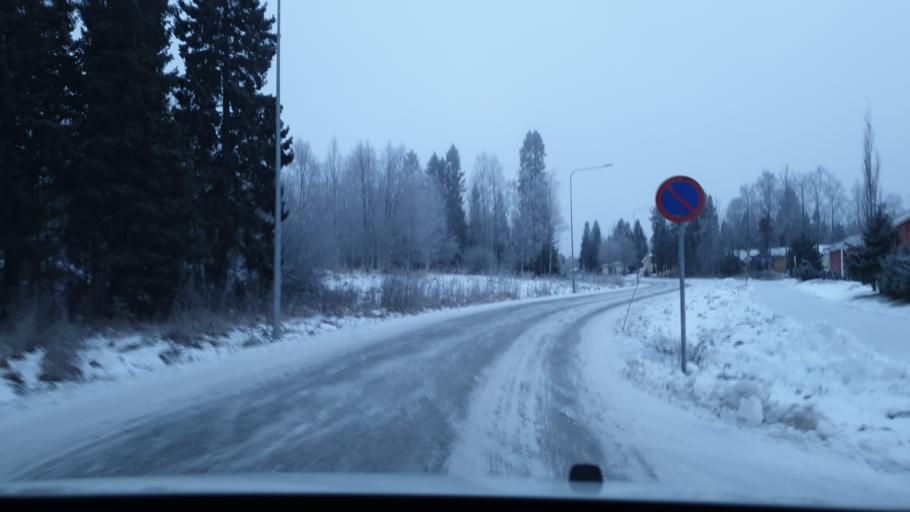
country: FI
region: Lapland
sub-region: Kemi-Tornio
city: Kemi
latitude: 65.7420
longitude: 24.6093
